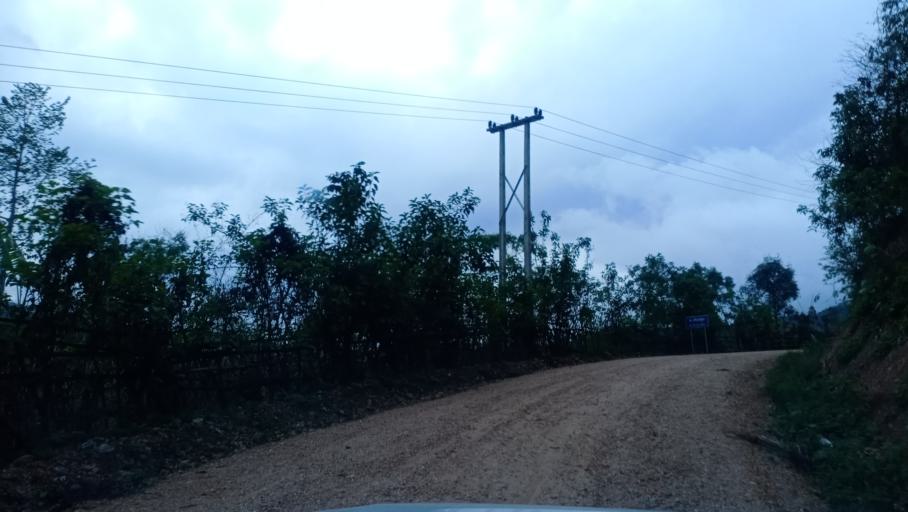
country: LA
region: Phongsali
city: Khoa
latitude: 21.2139
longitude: 102.6840
